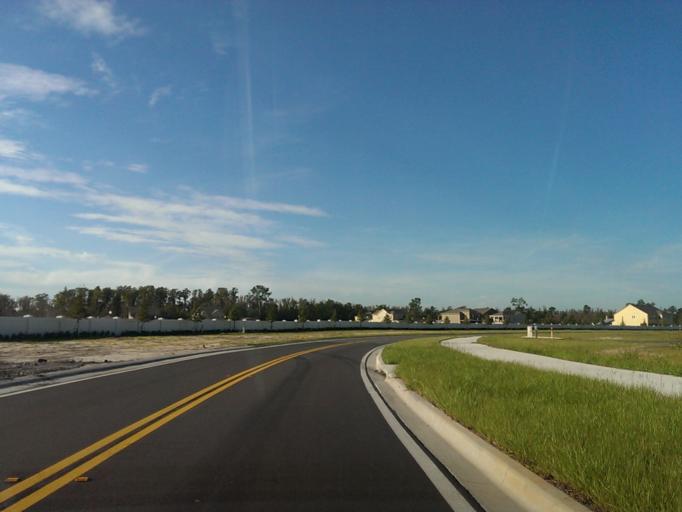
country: US
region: Florida
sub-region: Orange County
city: Lake Butler
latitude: 28.4333
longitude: -81.6052
